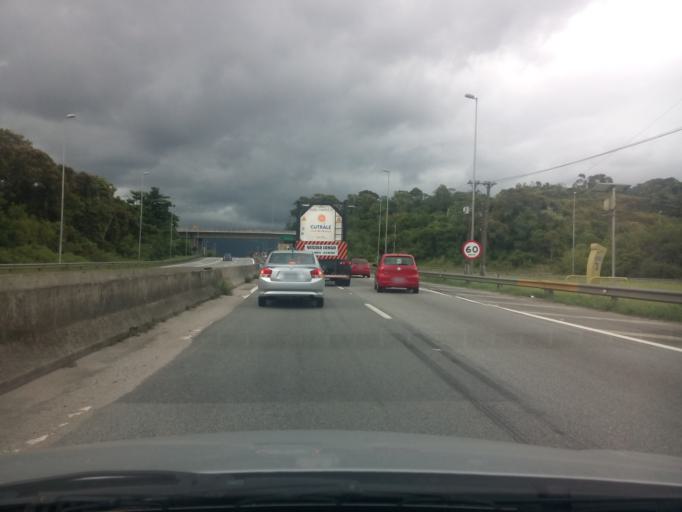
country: BR
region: Sao Paulo
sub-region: Santos
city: Santos
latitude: -23.9165
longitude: -46.2887
